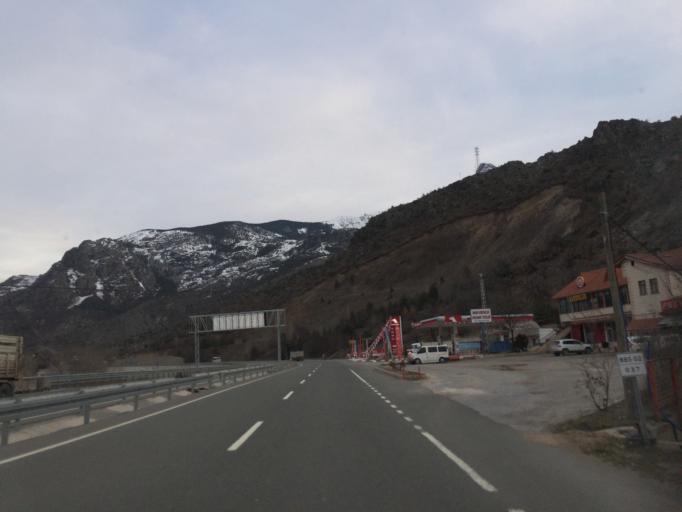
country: TR
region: Gumushane
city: Gumushkhane
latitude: 40.5071
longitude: 39.4226
